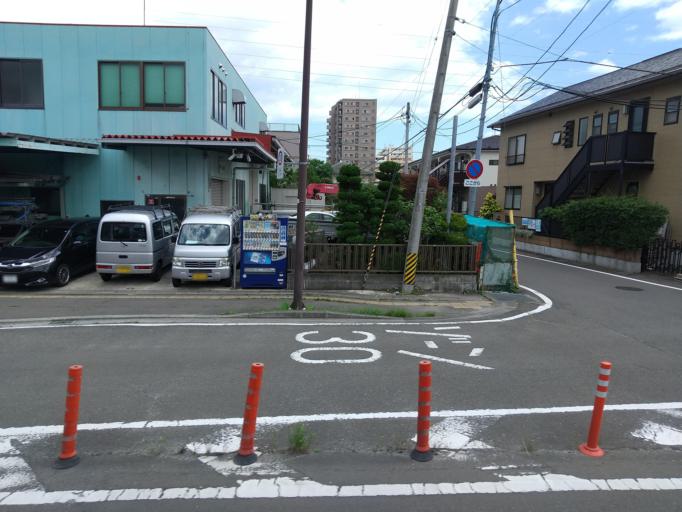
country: JP
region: Miyagi
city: Sendai-shi
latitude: 38.2746
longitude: 140.9302
